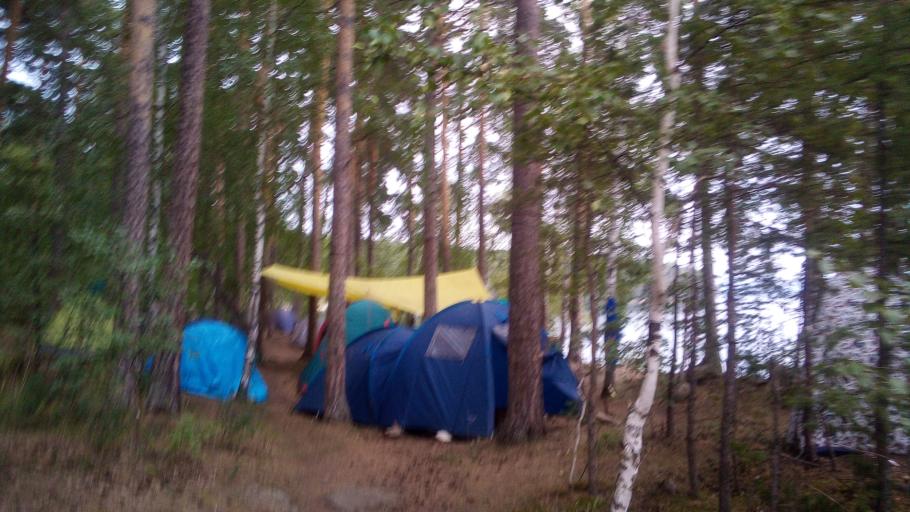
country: RU
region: Chelyabinsk
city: Turgoyak
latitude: 55.1773
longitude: 60.0286
